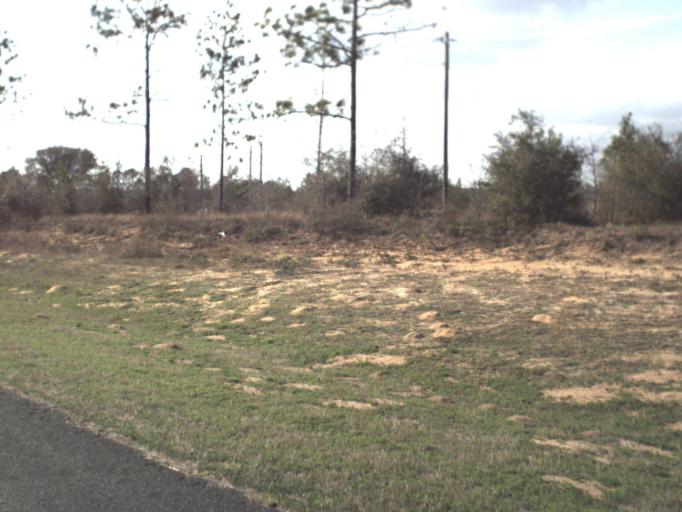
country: US
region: Florida
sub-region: Bay County
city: Youngstown
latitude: 30.4362
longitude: -85.4751
